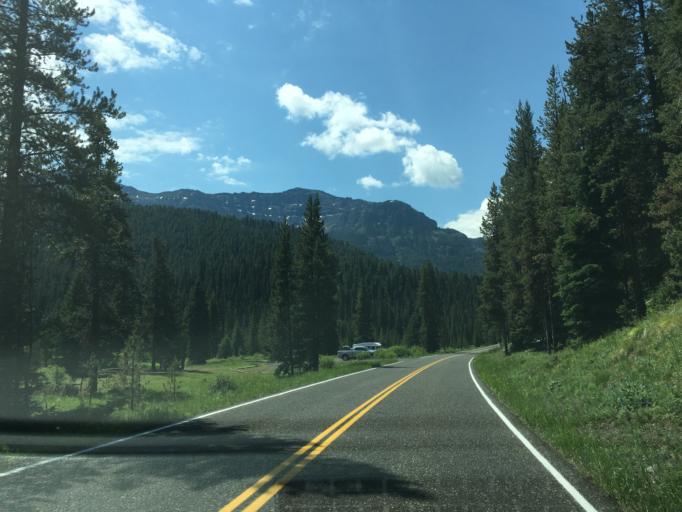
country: US
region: Montana
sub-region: Stillwater County
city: Absarokee
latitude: 44.9357
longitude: -110.0839
